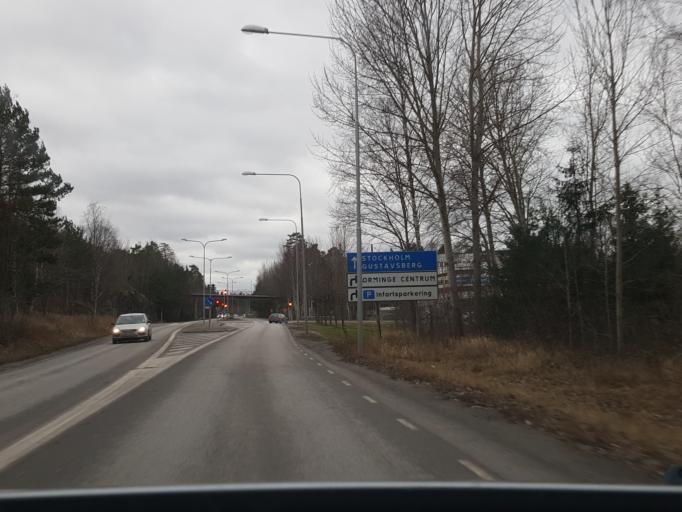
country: SE
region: Stockholm
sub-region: Nacka Kommun
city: Boo
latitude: 59.3277
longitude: 18.2617
